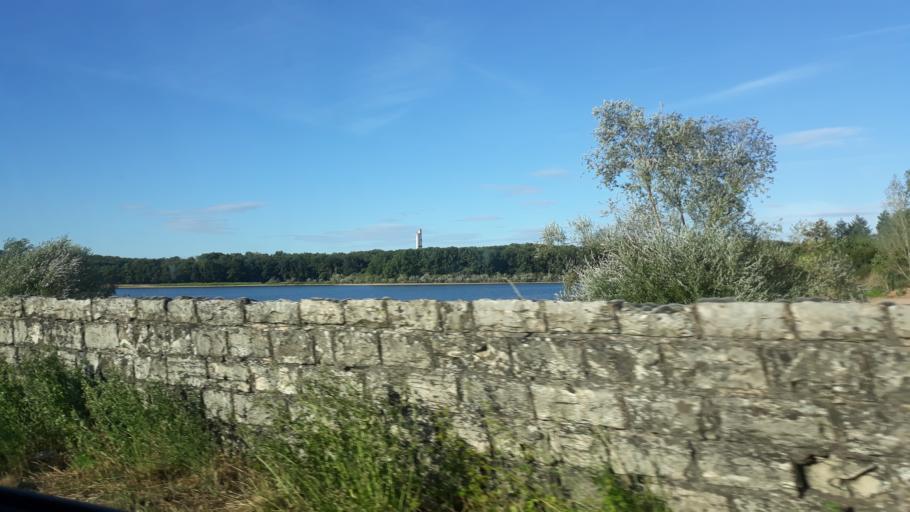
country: FR
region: Bourgogne
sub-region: Departement de Saone-et-Loire
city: Torcy
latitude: 46.7740
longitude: 4.4475
